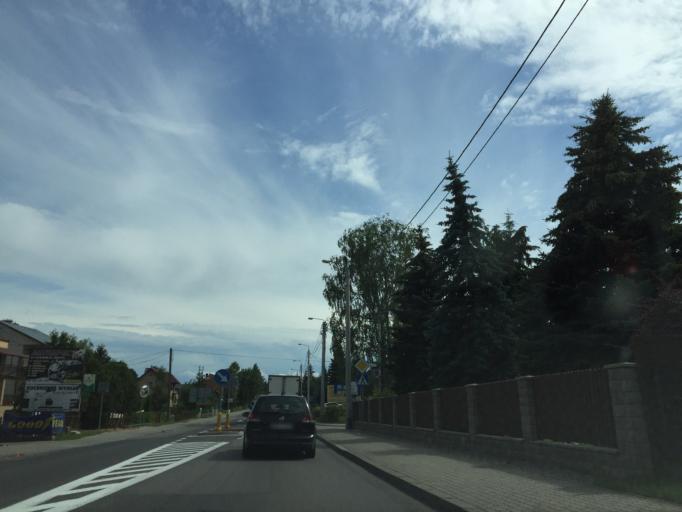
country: PL
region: Podlasie
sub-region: Powiat siemiatycki
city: Siemiatycze
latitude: 52.4160
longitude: 22.8691
